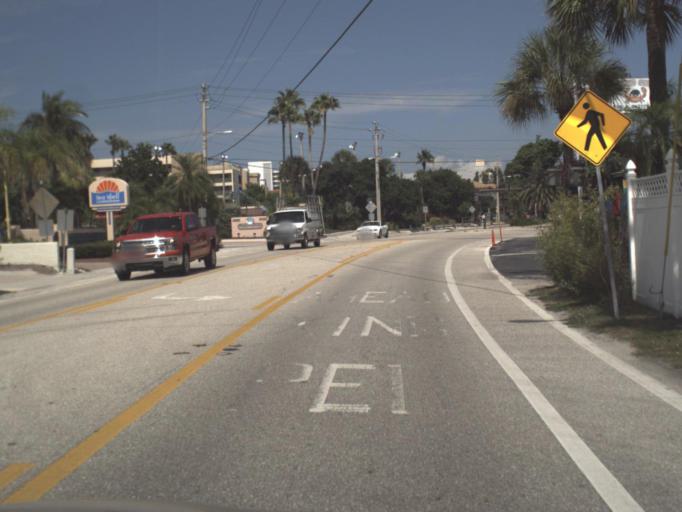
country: US
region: Florida
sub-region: Sarasota County
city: Gulf Gate Estates
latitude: 27.2509
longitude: -82.5346
